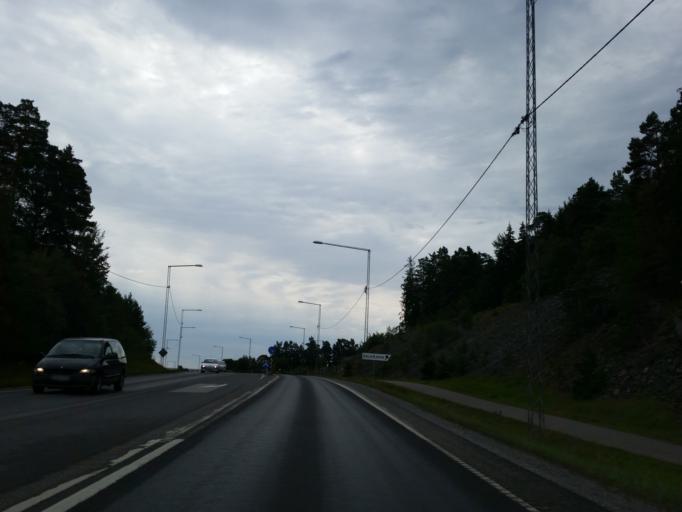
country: SE
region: Stockholm
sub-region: Botkyrka Kommun
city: Tumba
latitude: 59.2123
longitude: 17.8311
